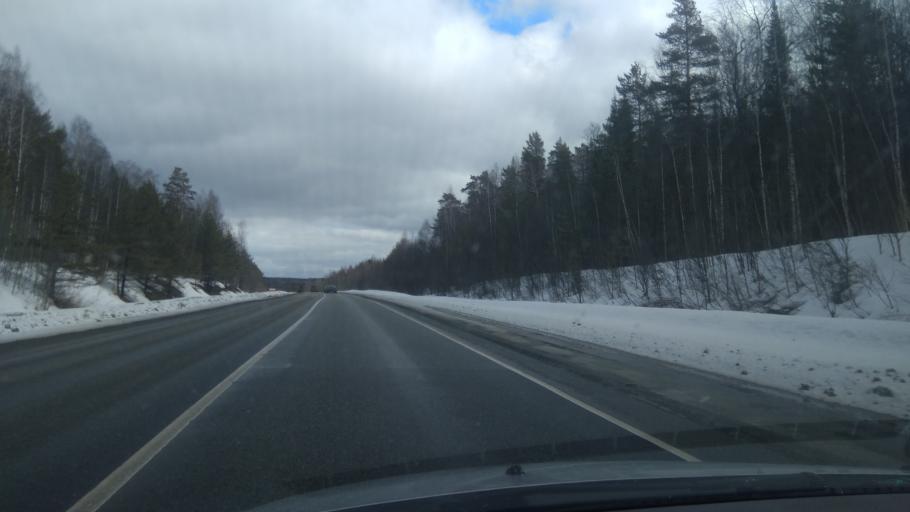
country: RU
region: Sverdlovsk
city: Bisert'
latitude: 56.8344
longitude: 58.8930
